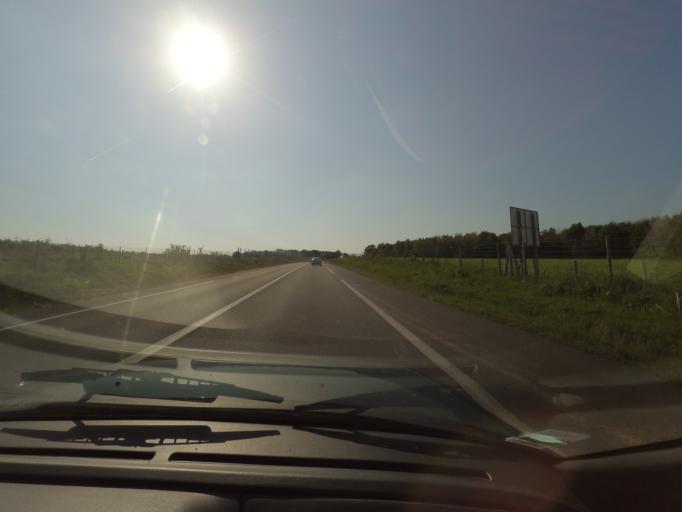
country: FR
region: Pays de la Loire
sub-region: Departement de la Vendee
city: Moutiers-les-Mauxfaits
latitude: 46.4769
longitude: -1.4248
